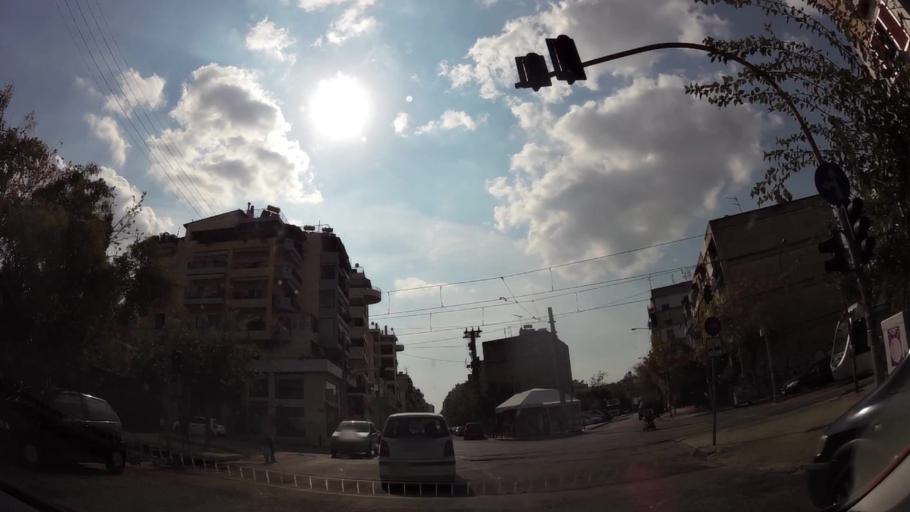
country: GR
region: Attica
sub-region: Nomarchia Athinas
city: Dhafni
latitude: 37.9584
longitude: 23.7251
